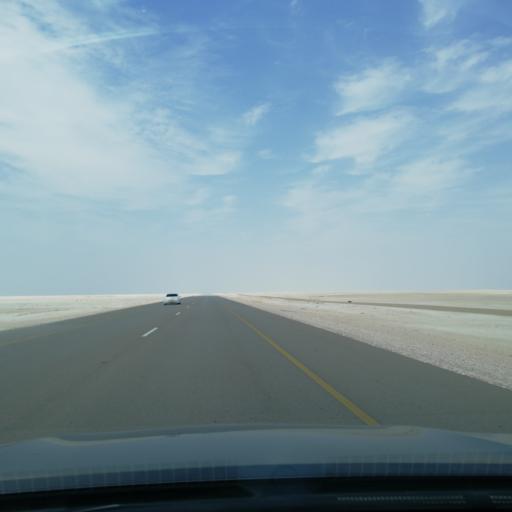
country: OM
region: Al Wusta
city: Hayma'
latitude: 20.1937
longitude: 56.5401
